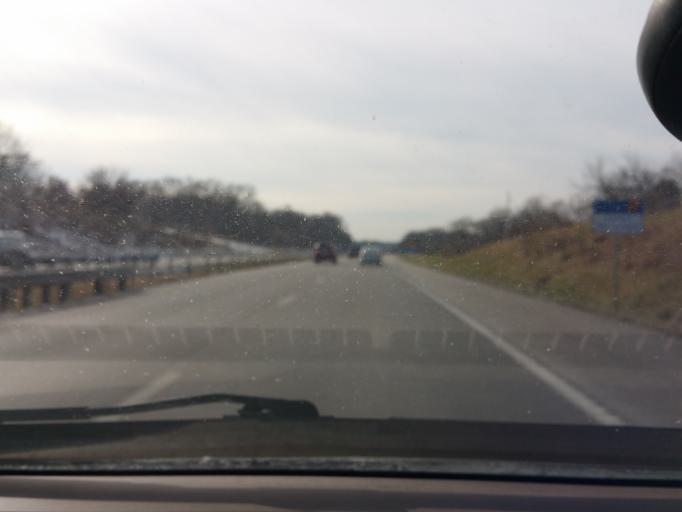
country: US
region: Missouri
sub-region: Clay County
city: Claycomo
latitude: 39.1836
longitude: -94.5214
